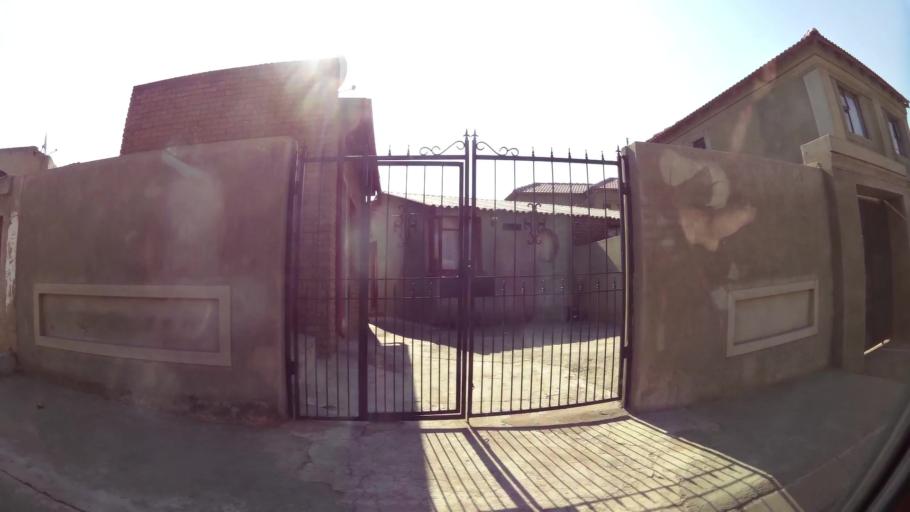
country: ZA
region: Gauteng
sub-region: City of Johannesburg Metropolitan Municipality
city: Soweto
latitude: -26.2508
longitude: 27.9352
